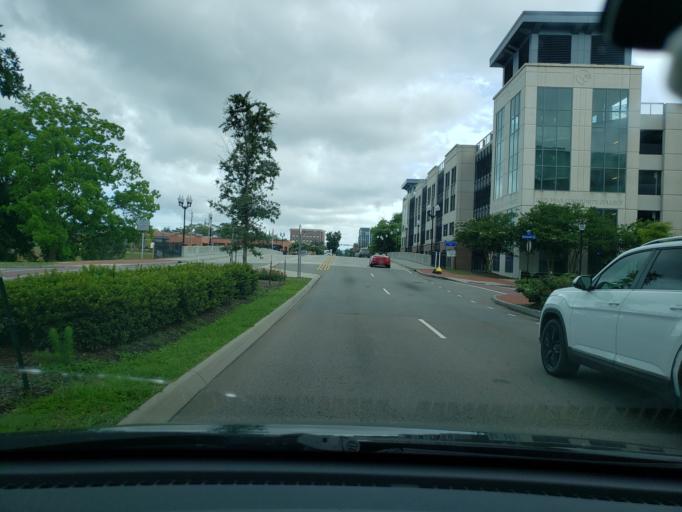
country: US
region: North Carolina
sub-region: New Hanover County
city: Wilmington
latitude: 34.2437
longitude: -77.9470
